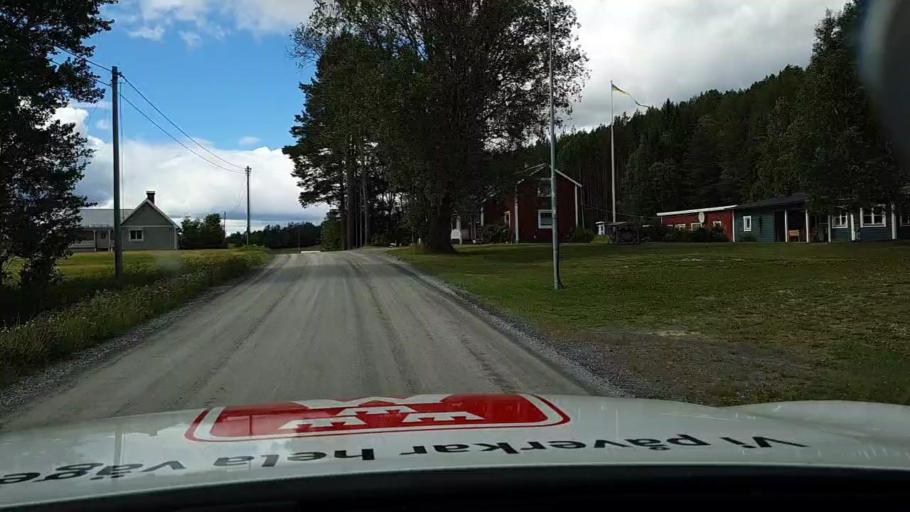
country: SE
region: Jaemtland
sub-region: Krokoms Kommun
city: Krokom
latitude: 63.5677
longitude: 14.2631
